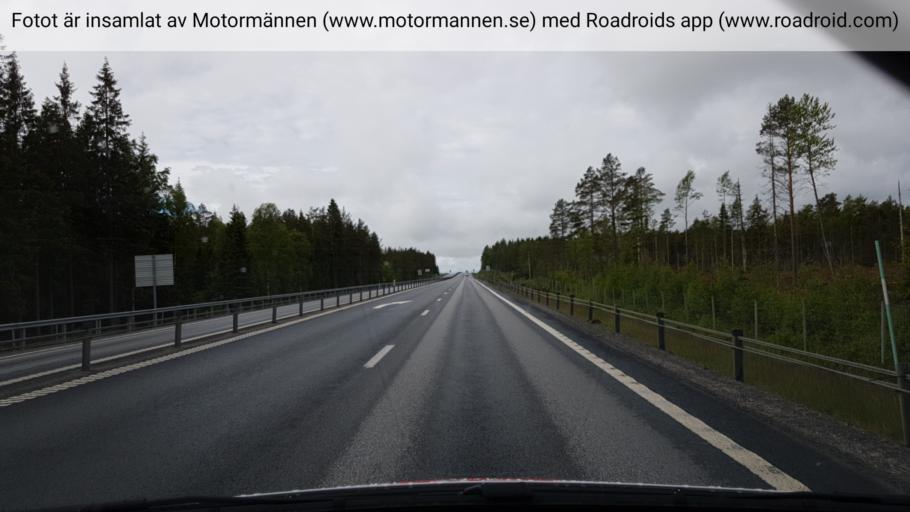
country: SE
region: Vaesterbotten
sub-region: Umea Kommun
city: Hoernefors
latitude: 63.6943
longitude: 20.0249
